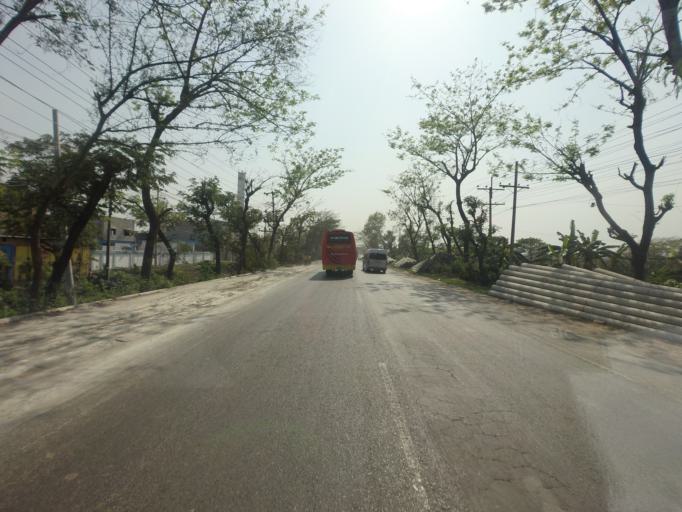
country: BD
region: Dhaka
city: Paltan
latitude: 23.7996
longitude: 90.5826
